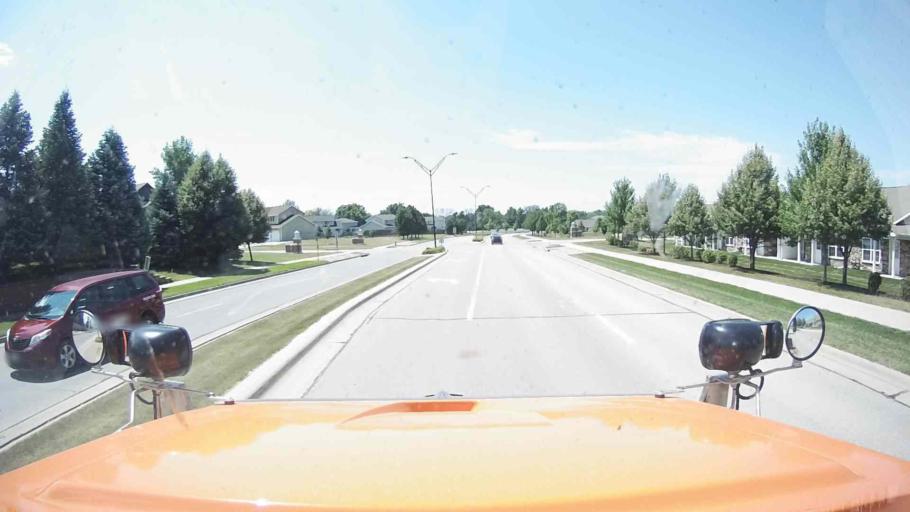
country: US
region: Iowa
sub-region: Polk County
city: Altoona
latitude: 41.6609
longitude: -93.4700
